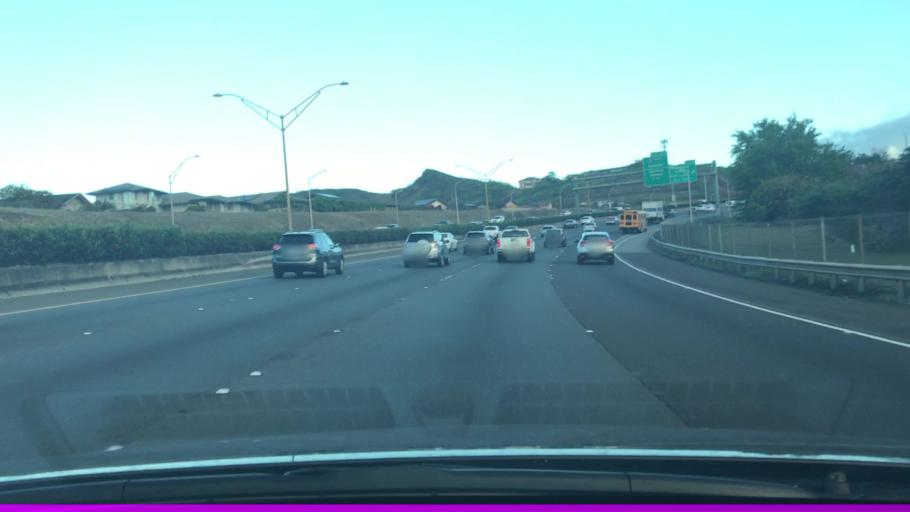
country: US
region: Hawaii
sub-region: Honolulu County
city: Halawa Heights
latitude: 21.3561
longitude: -157.8983
